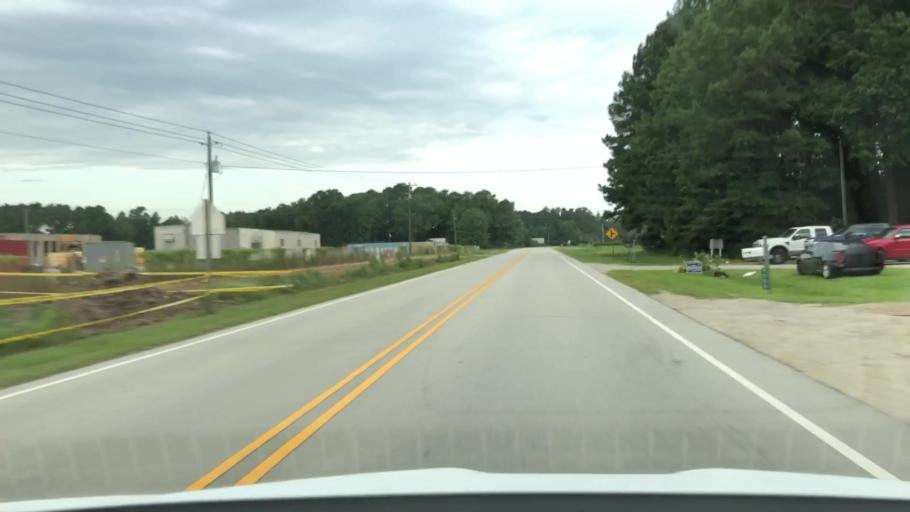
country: US
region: North Carolina
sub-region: Jones County
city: Trenton
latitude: 35.0353
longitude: -77.3365
